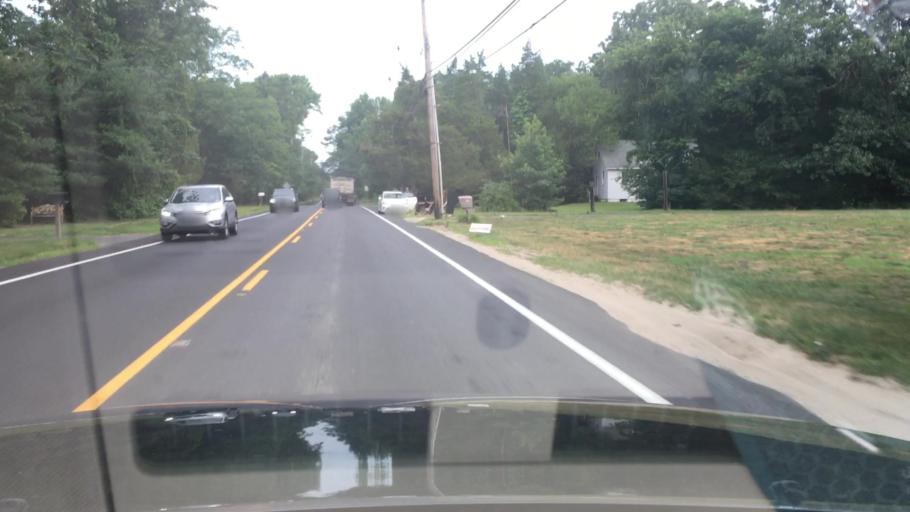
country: US
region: New Jersey
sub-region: Ocean County
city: Cedar Glen West
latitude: 40.0504
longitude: -74.3343
